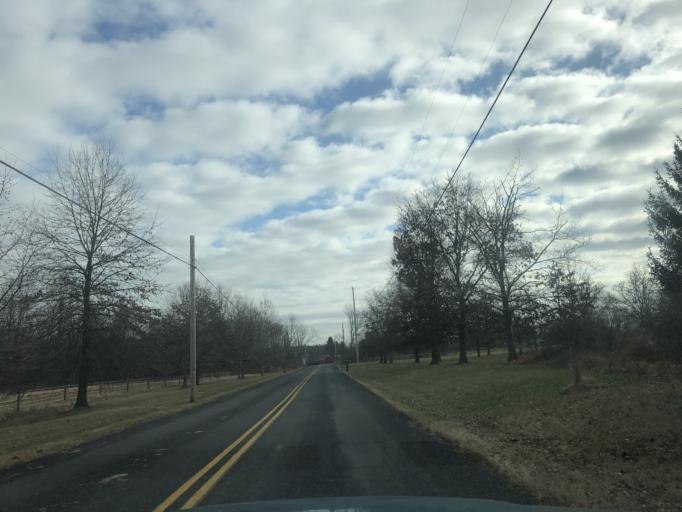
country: US
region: Pennsylvania
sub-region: Bucks County
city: Spinnerstown
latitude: 40.4449
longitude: -75.4185
